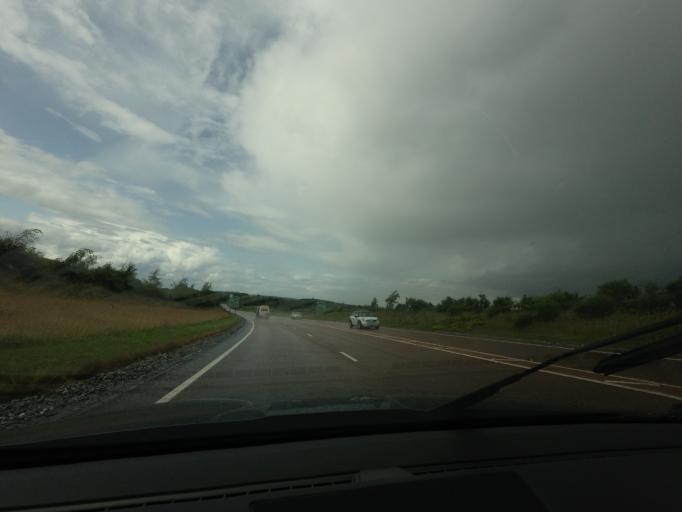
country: GB
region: Scotland
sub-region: Moray
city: Fochabers
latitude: 57.6129
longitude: -3.0868
